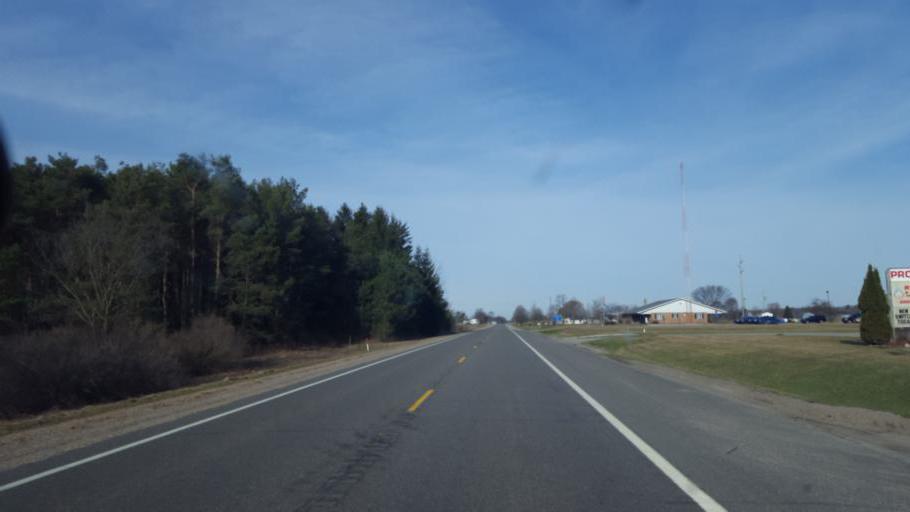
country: US
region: Michigan
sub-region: Montcalm County
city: Lakeview
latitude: 43.4314
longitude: -85.2858
